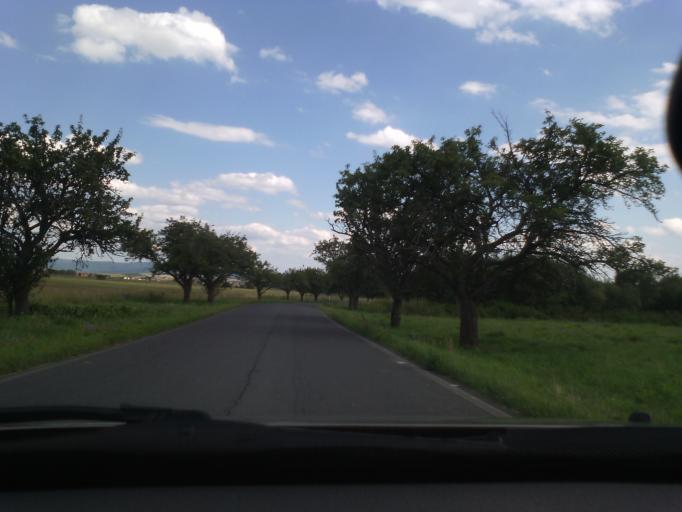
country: SK
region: Presovsky
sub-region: Okres Poprad
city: Nova Lesna
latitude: 49.1304
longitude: 20.3202
